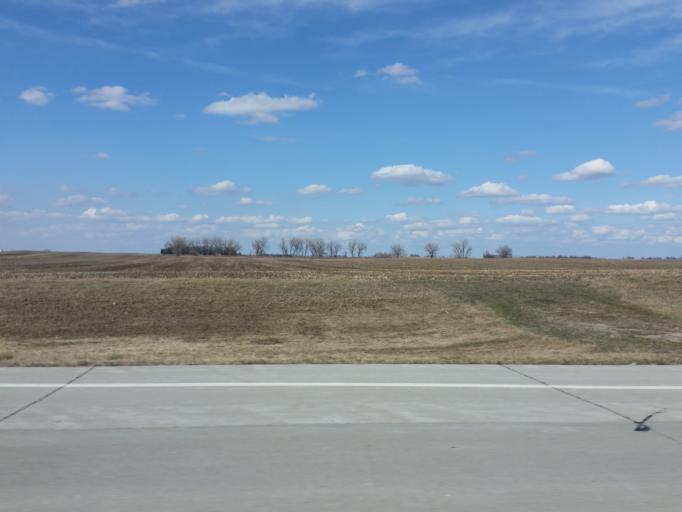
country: US
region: Minnesota
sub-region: Lac qui Parle County
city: Madison
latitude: 44.9359
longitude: -96.1632
